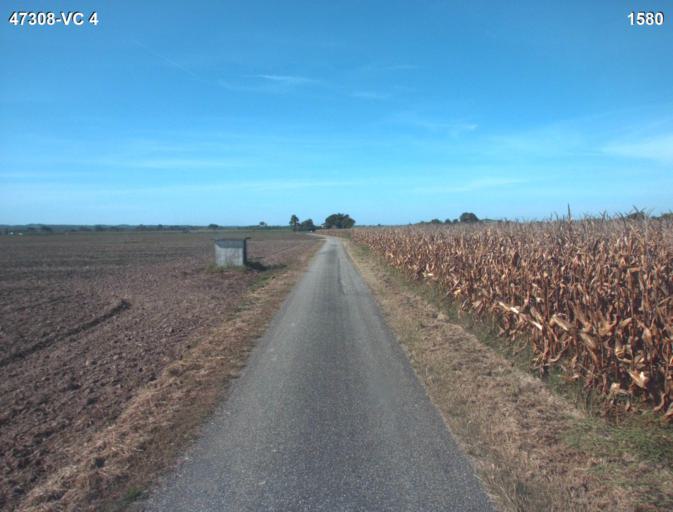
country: FR
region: Aquitaine
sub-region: Departement du Lot-et-Garonne
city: Buzet-sur-Baise
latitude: 44.2676
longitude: 0.3295
